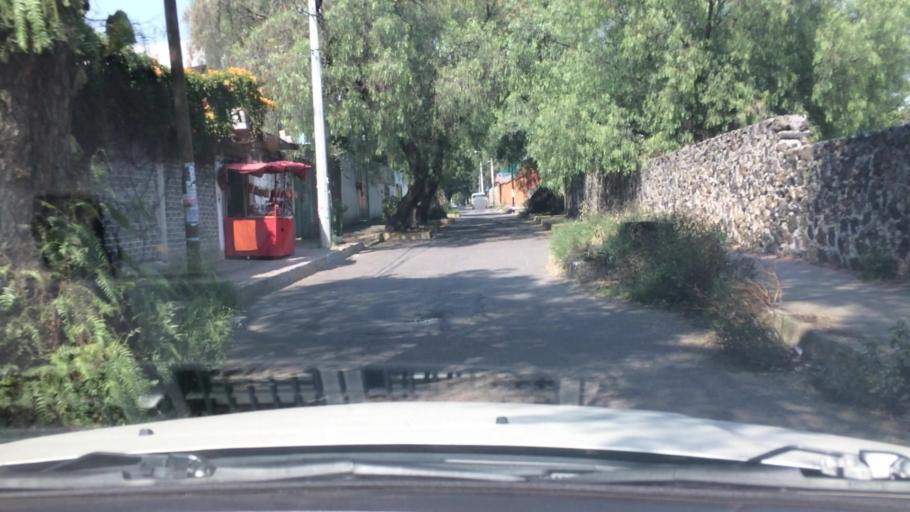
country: MX
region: Mexico City
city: Xochimilco
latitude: 19.2617
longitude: -99.1335
